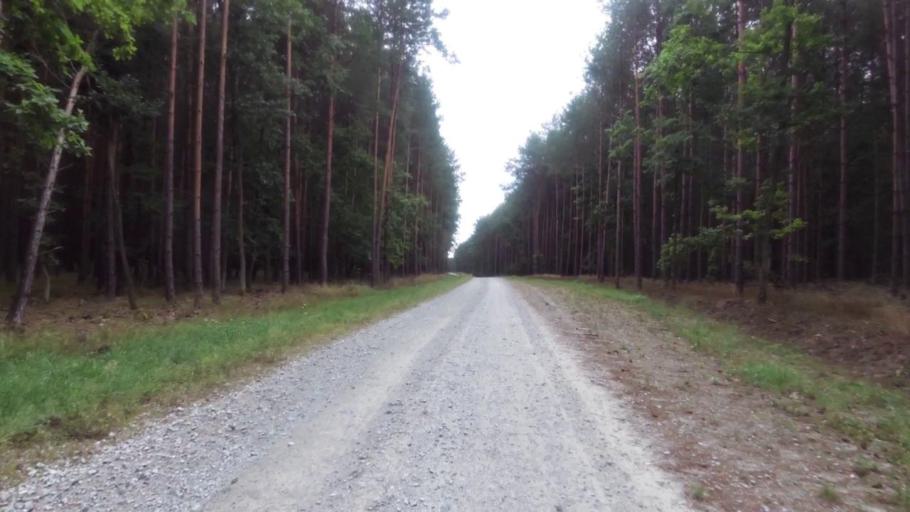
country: PL
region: West Pomeranian Voivodeship
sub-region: Powiat mysliborski
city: Boleszkowice
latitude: 52.6644
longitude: 14.6199
